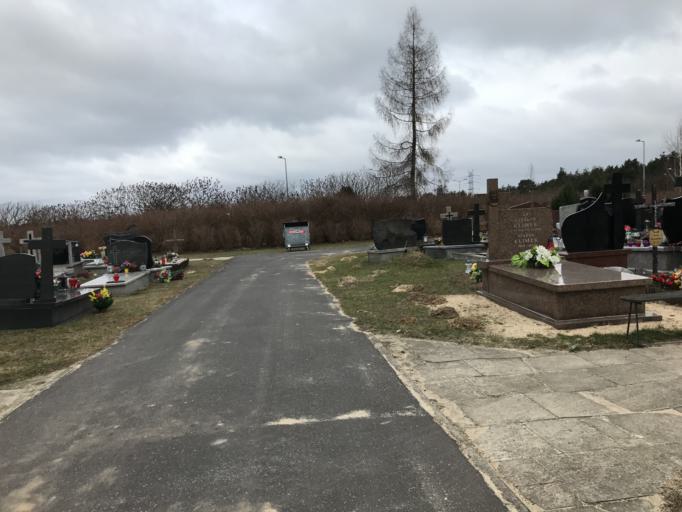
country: PL
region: Masovian Voivodeship
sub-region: Powiat warszawski zachodni
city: Lomianki
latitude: 52.3040
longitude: 20.8871
